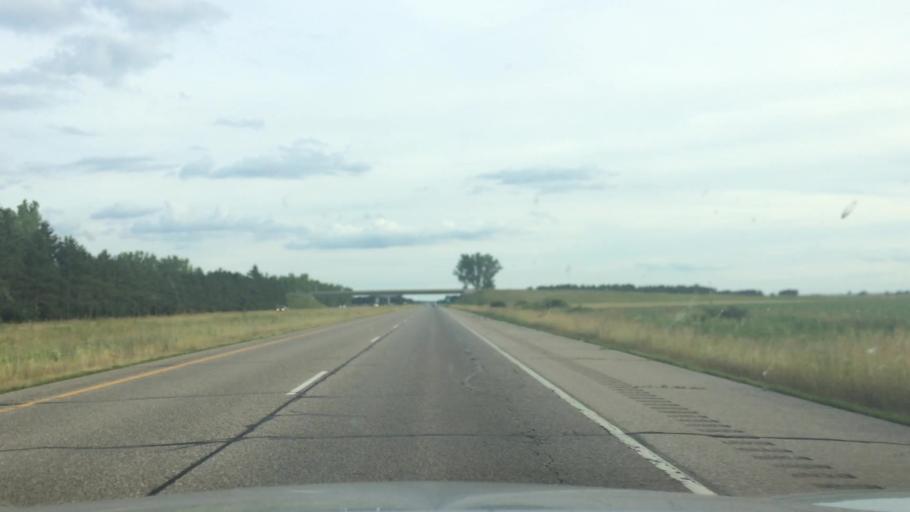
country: US
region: Wisconsin
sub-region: Waushara County
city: Wautoma
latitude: 44.1592
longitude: -89.5327
